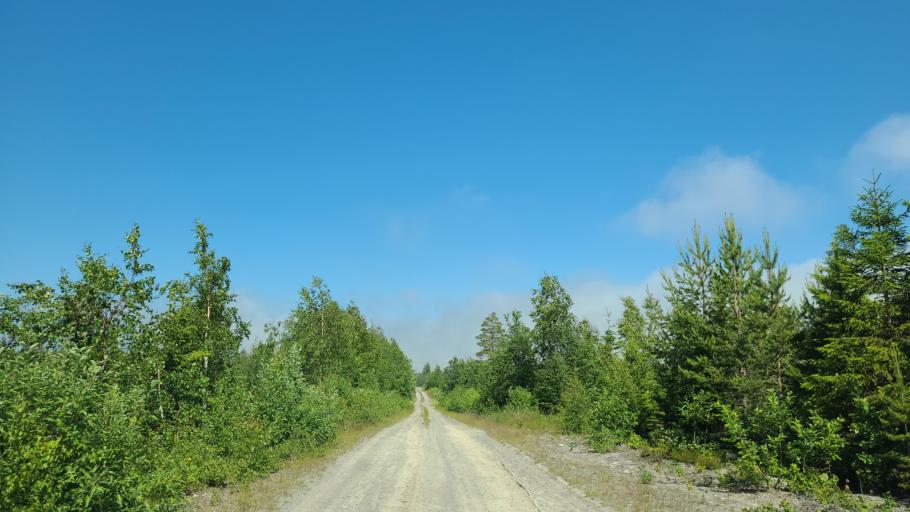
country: SE
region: Vaesternorrland
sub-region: OErnskoeldsviks Kommun
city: Husum
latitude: 63.4394
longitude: 19.2331
